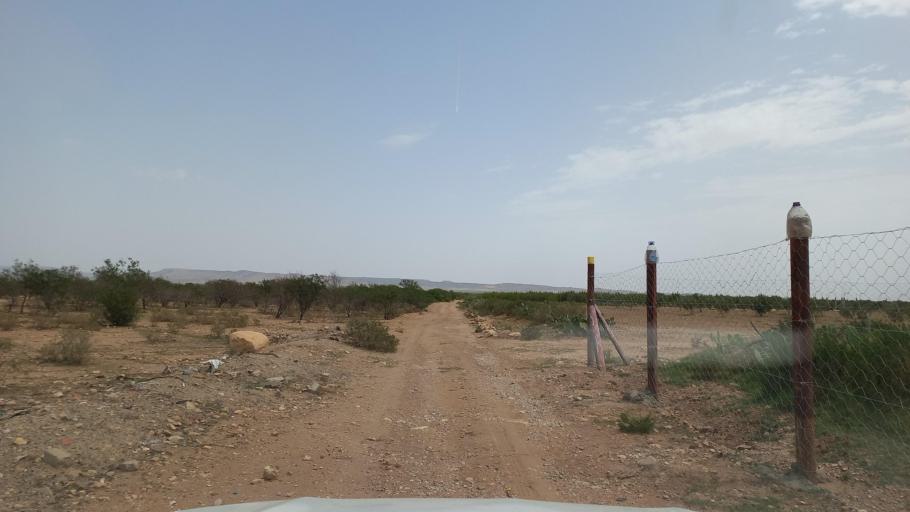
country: TN
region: Al Qasrayn
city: Kasserine
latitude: 35.2929
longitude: 9.0098
